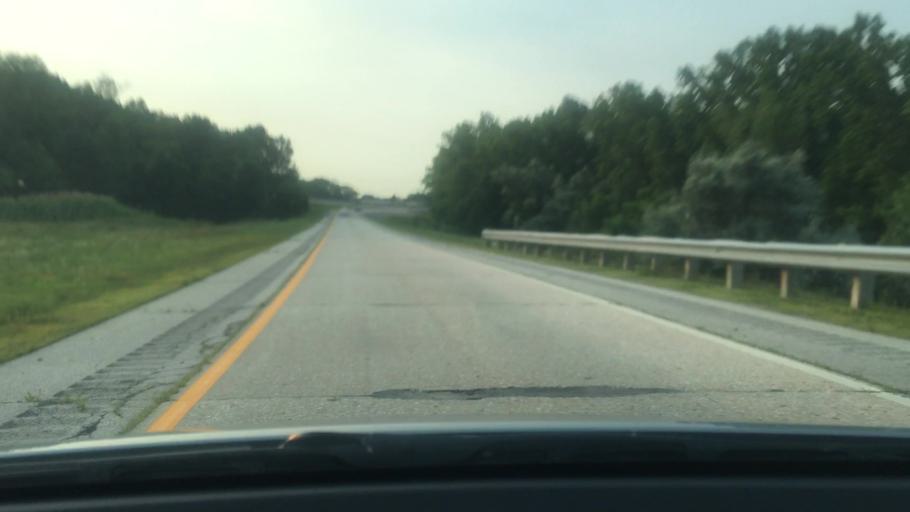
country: US
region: Wisconsin
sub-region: Brown County
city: Ashwaubenon
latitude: 44.4839
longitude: -88.0838
